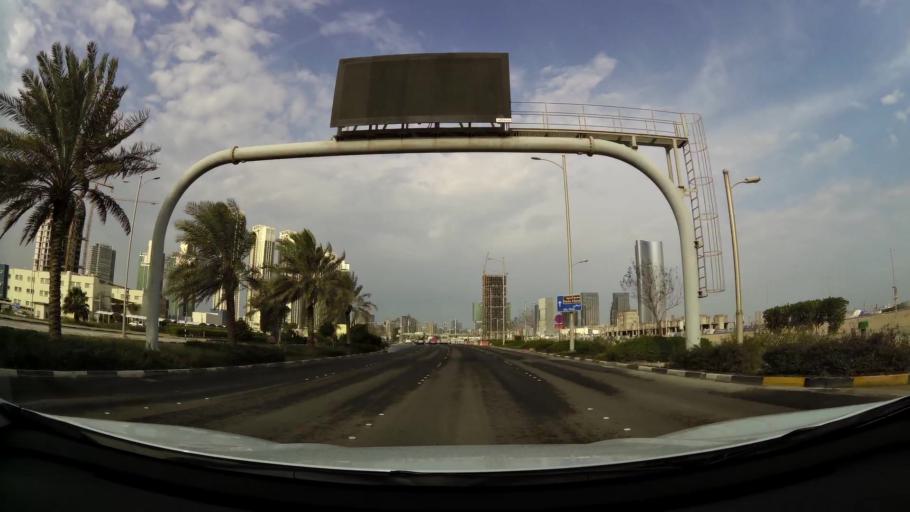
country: AE
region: Abu Dhabi
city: Abu Dhabi
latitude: 24.4923
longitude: 54.4026
